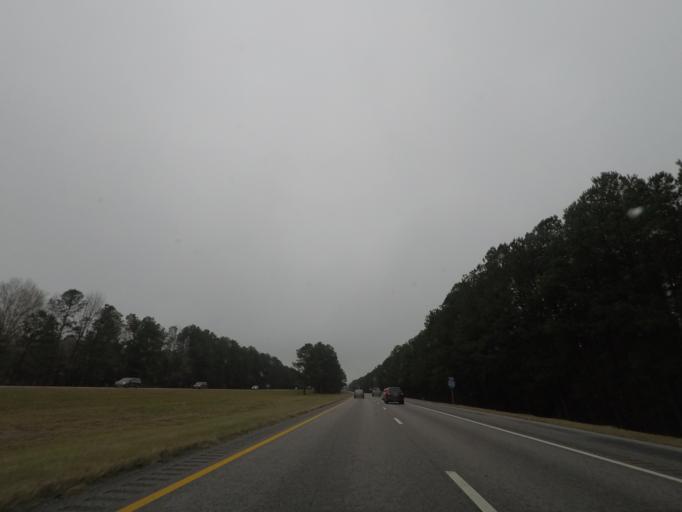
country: US
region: South Carolina
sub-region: Sumter County
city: East Sumter
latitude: 33.8954
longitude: -80.0964
